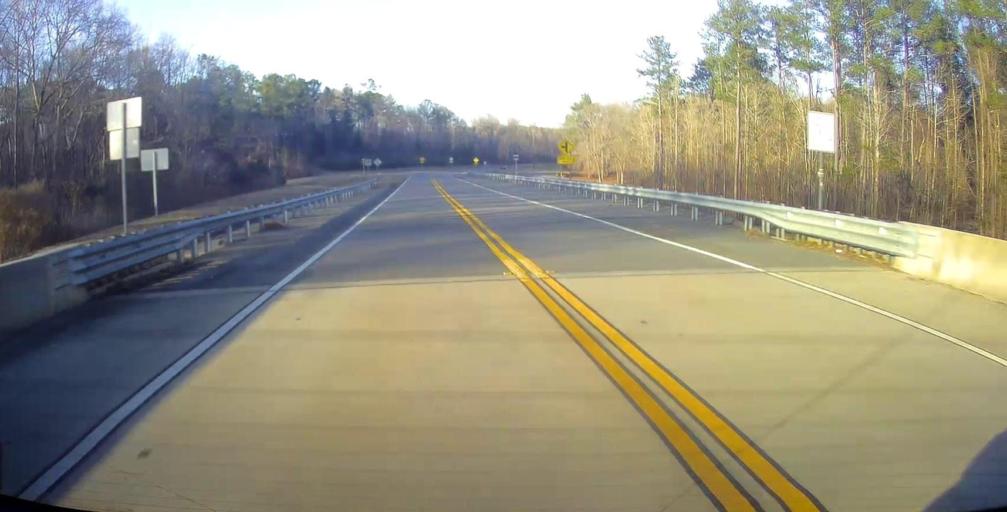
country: US
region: Georgia
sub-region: Upson County
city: Thomaston
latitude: 32.8389
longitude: -84.4244
